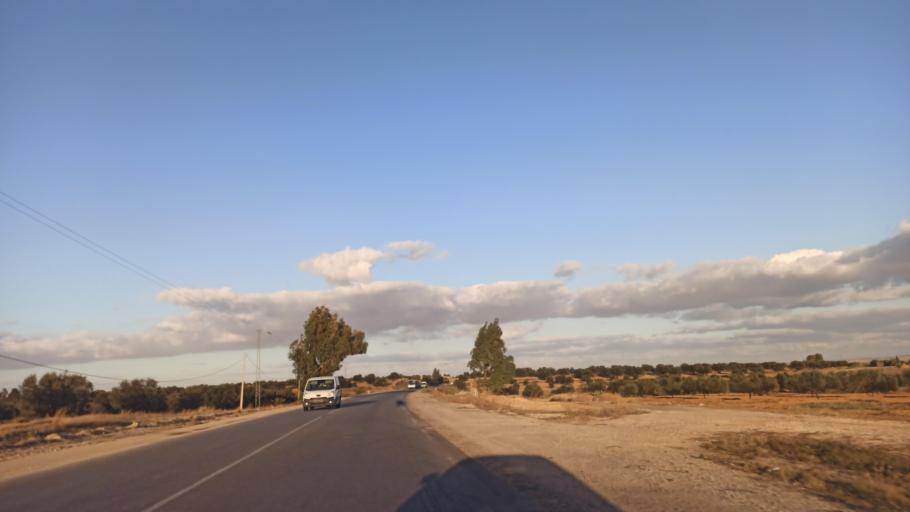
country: TN
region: Al Qayrawan
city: Sbikha
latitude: 35.8760
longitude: 10.2222
